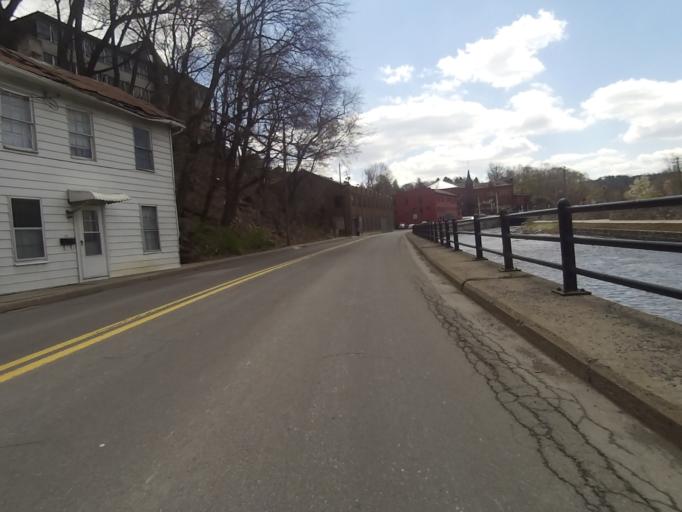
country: US
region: Pennsylvania
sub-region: Centre County
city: Bellefonte
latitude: 40.9132
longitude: -77.7812
